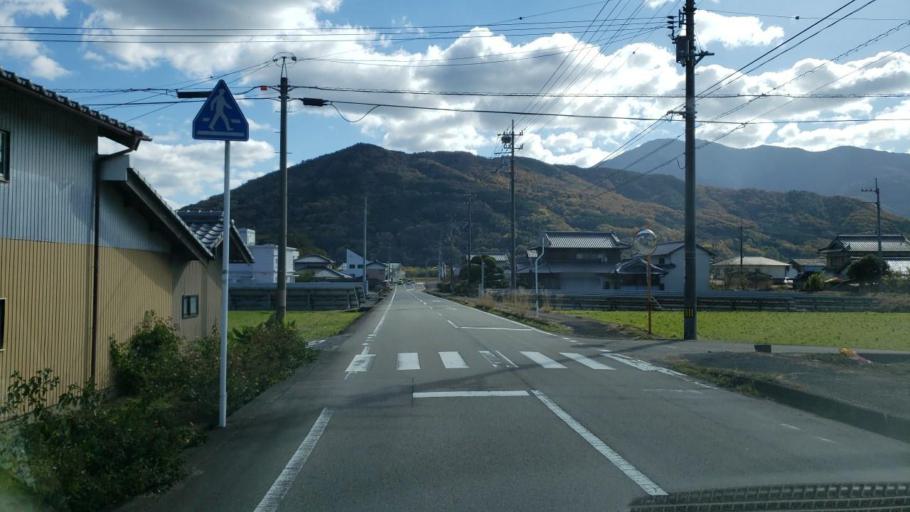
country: JP
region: Tokushima
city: Wakimachi
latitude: 34.0692
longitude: 134.1807
